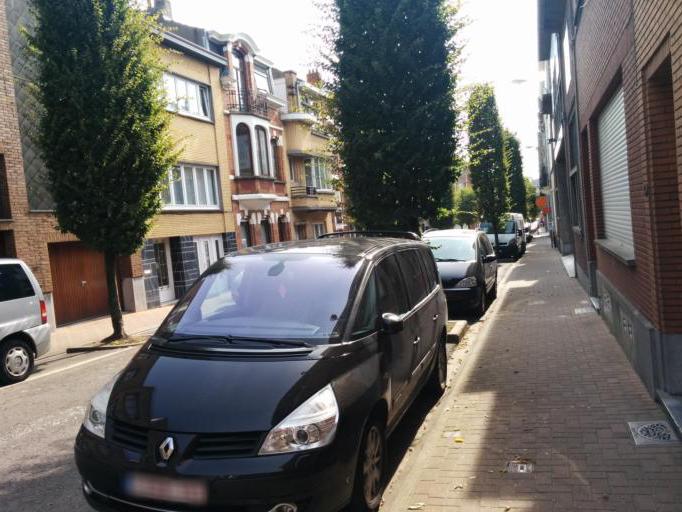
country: BE
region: Brussels Capital
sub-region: Bruxelles-Capitale
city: Brussels
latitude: 50.8724
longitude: 4.3302
